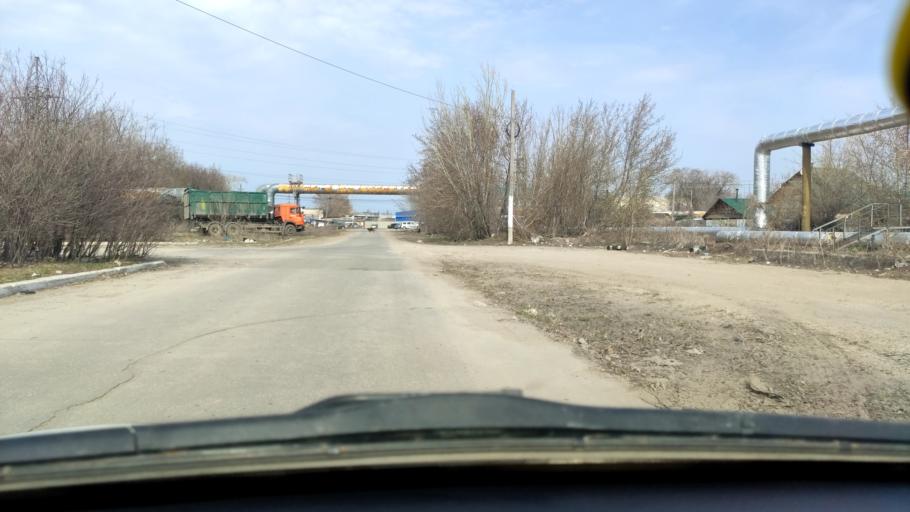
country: RU
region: Samara
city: Tol'yatti
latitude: 53.5454
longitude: 49.4325
